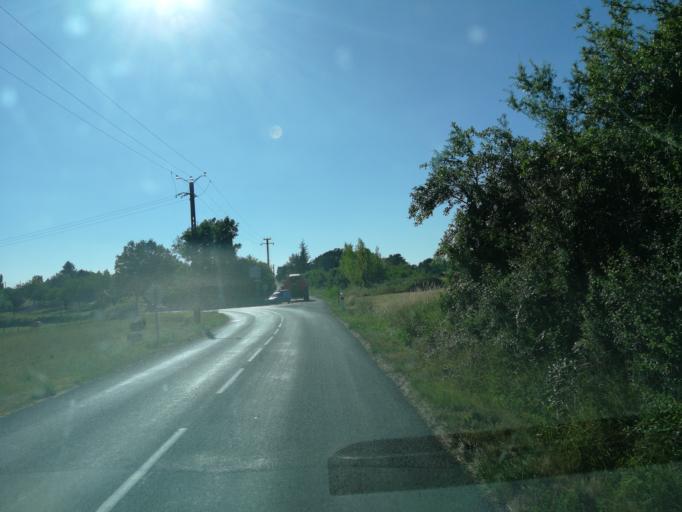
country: FR
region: Midi-Pyrenees
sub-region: Departement du Lot
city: Gourdon
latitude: 44.7187
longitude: 1.3606
